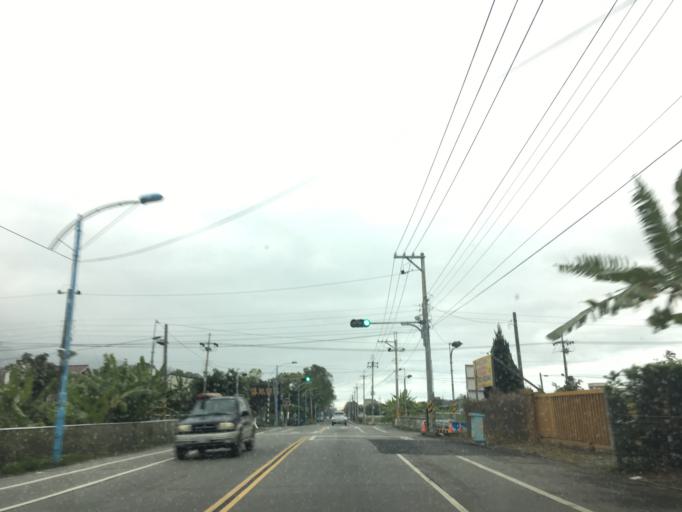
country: TW
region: Taiwan
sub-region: Hualien
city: Hualian
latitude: 23.9828
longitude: 121.5693
